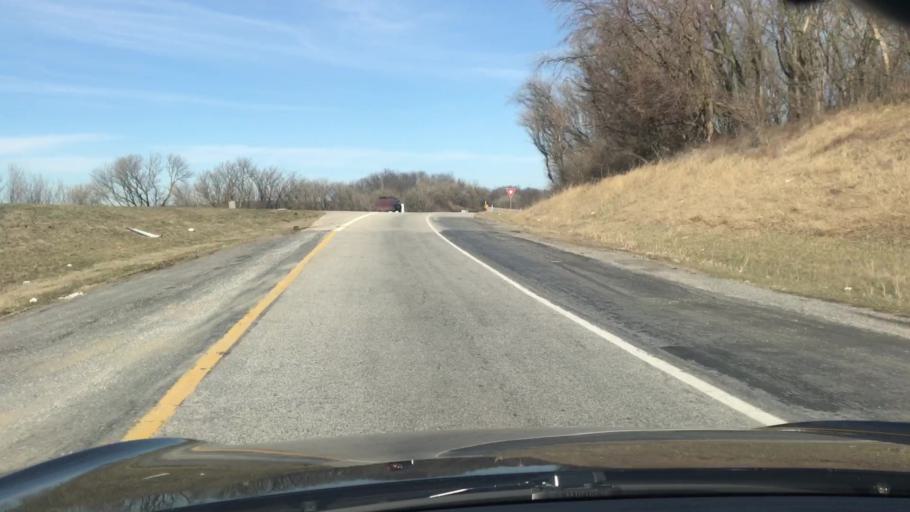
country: US
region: Pennsylvania
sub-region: Cumberland County
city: Newville
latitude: 40.1293
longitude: -77.3486
